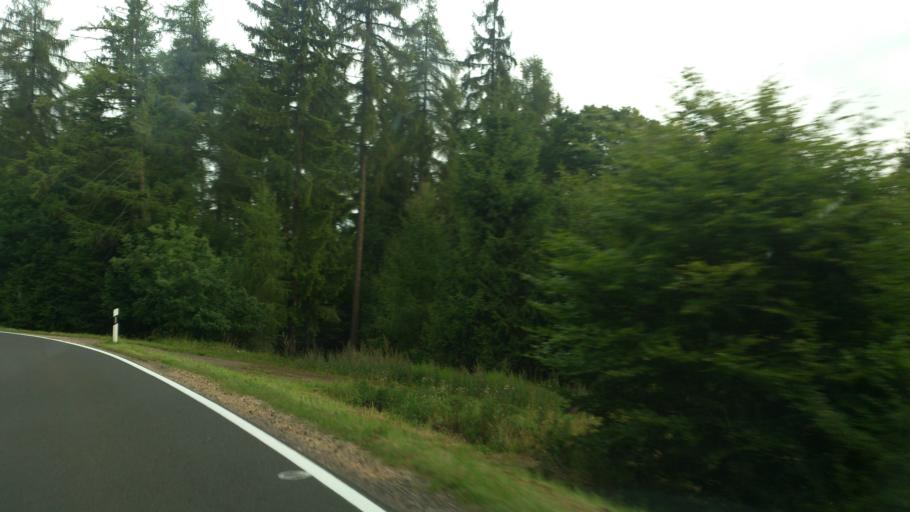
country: DE
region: Rheinland-Pfalz
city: Nohn
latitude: 50.3155
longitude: 6.7957
